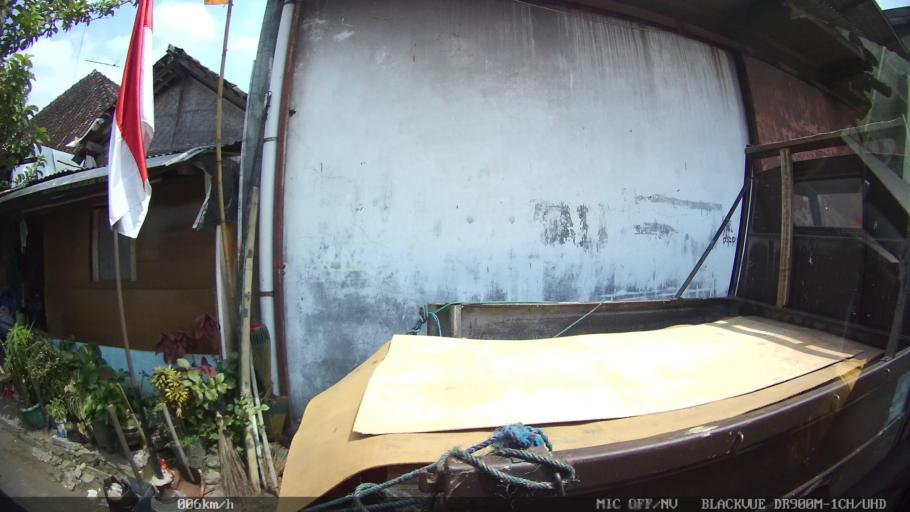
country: ID
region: Daerah Istimewa Yogyakarta
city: Yogyakarta
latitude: -7.8026
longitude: 110.3859
